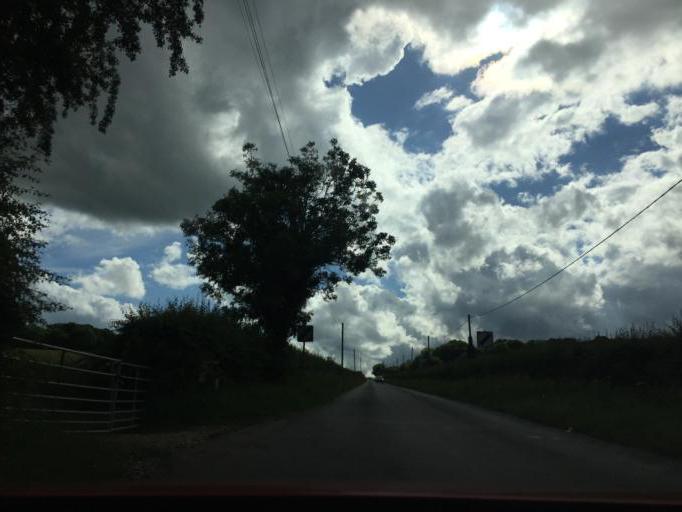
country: GB
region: England
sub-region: Hertfordshire
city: Harpenden
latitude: 51.8493
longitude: -0.3762
